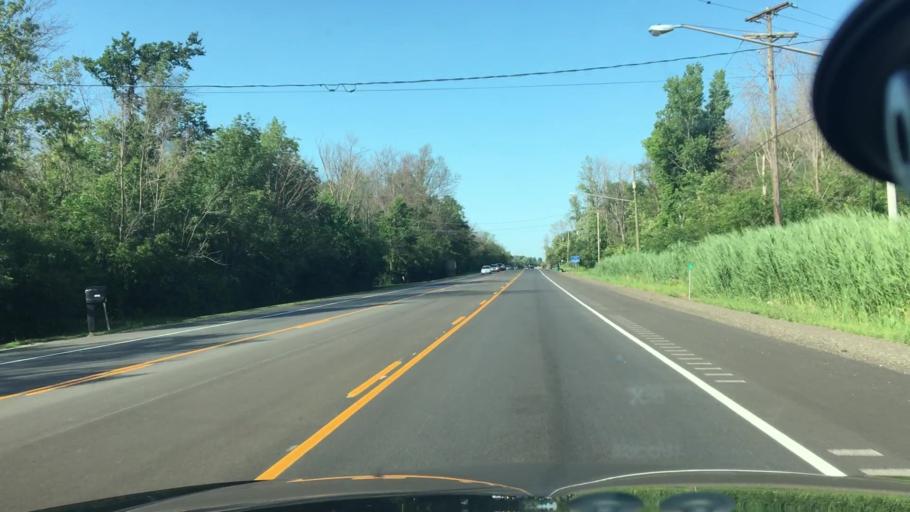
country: US
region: New York
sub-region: Erie County
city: Wanakah
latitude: 42.7293
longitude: -78.8874
